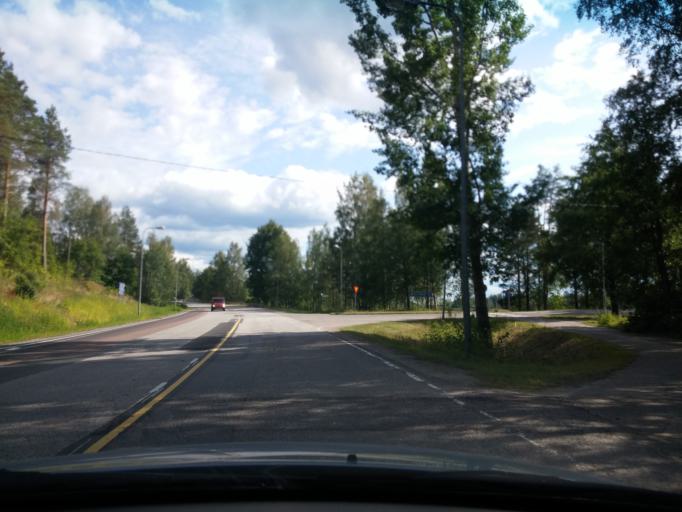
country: FI
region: Central Finland
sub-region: Keuruu
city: Keuruu
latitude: 62.2712
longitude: 24.6892
